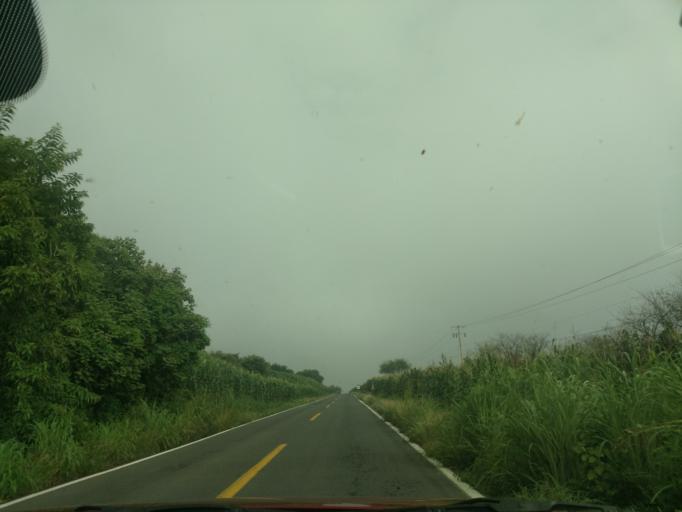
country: MX
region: Jalisco
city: Ameca
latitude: 20.5407
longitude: -104.1430
